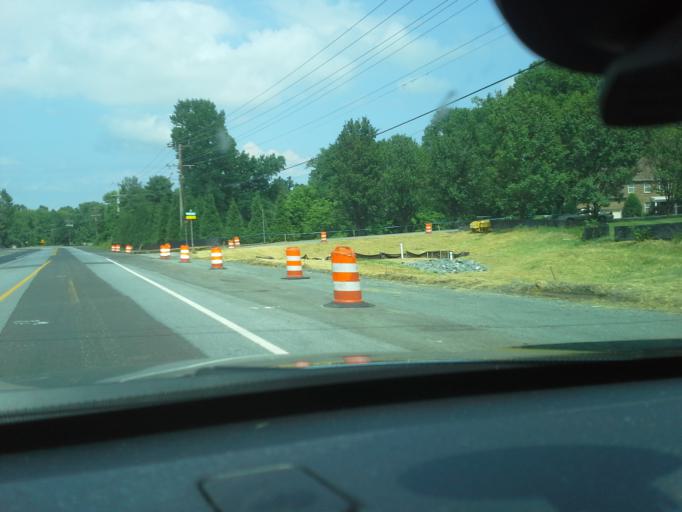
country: US
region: Maryland
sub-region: Anne Arundel County
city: Davidsonville
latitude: 38.8759
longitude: -76.6093
